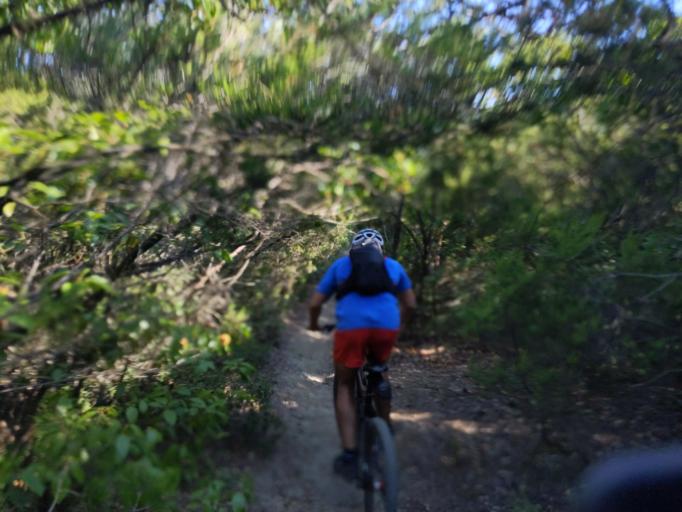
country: ES
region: Catalonia
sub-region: Provincia de Barcelona
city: Cerdanyola del Valles
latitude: 41.4644
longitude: 2.1341
